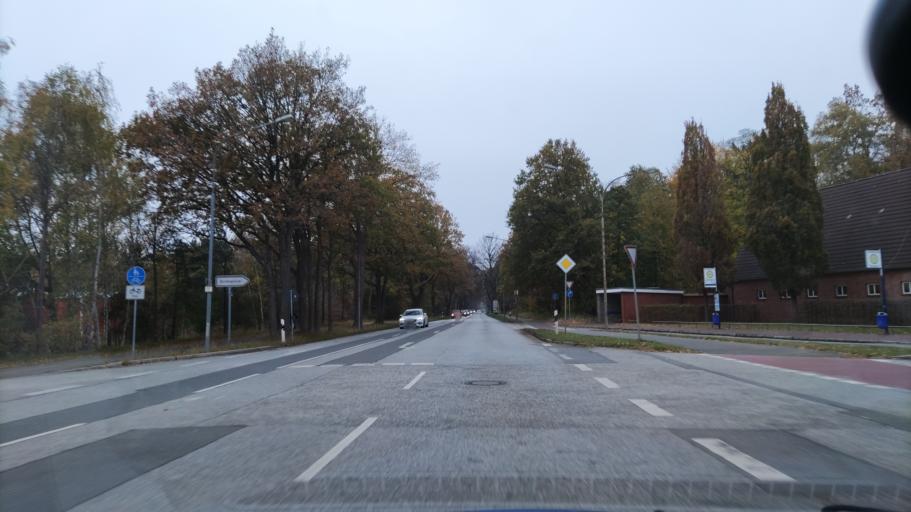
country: DE
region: Schleswig-Holstein
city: Gross Gronau
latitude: 53.8250
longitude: 10.7212
